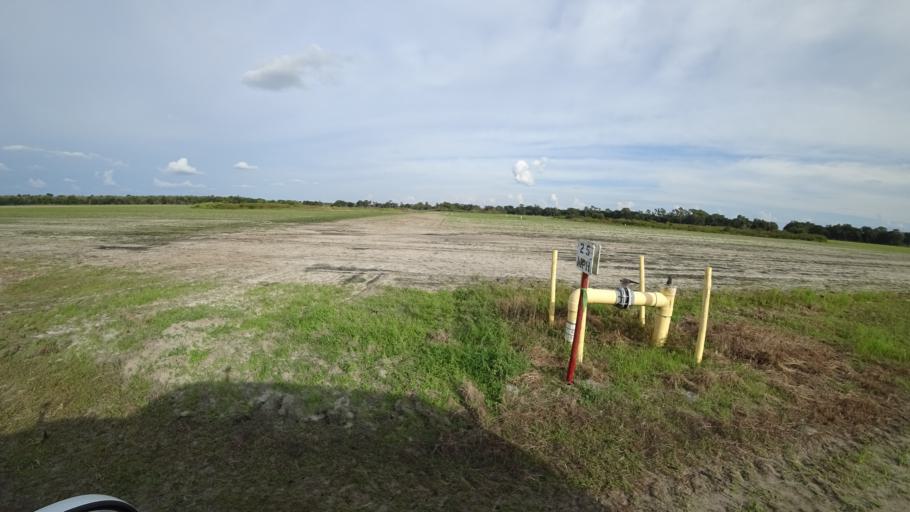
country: US
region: Florida
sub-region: Hillsborough County
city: Wimauma
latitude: 27.5563
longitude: -82.0955
